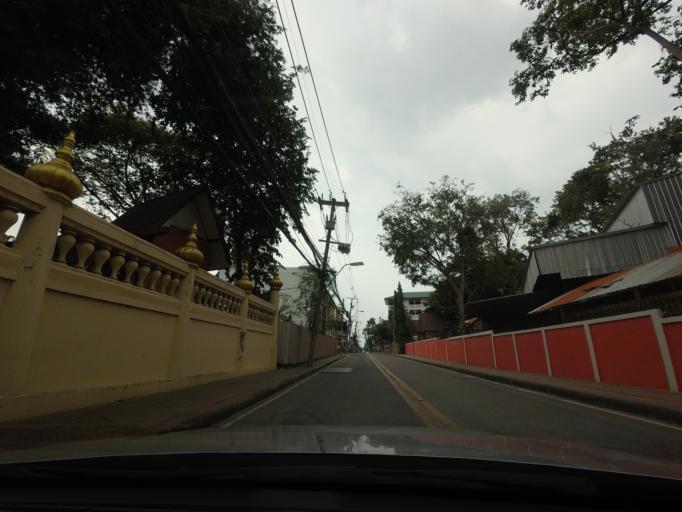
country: TH
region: Chon Buri
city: Phatthaya
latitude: 12.9625
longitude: 100.8936
